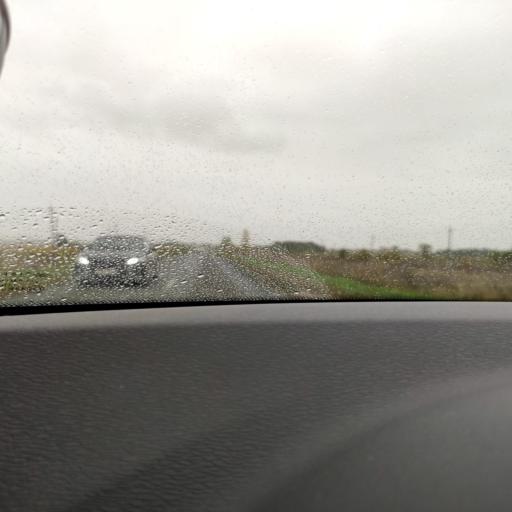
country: RU
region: Samara
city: Yelkhovka
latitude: 53.7405
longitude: 50.2762
